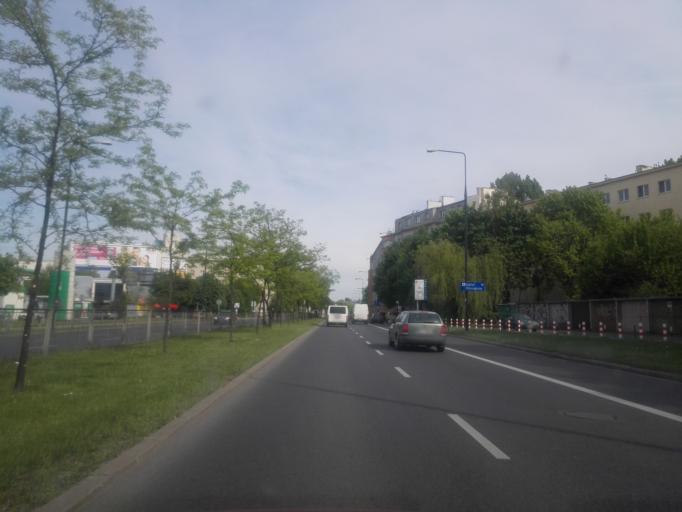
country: PL
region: Masovian Voivodeship
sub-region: Warszawa
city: Ochota
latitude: 52.2184
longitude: 20.9747
